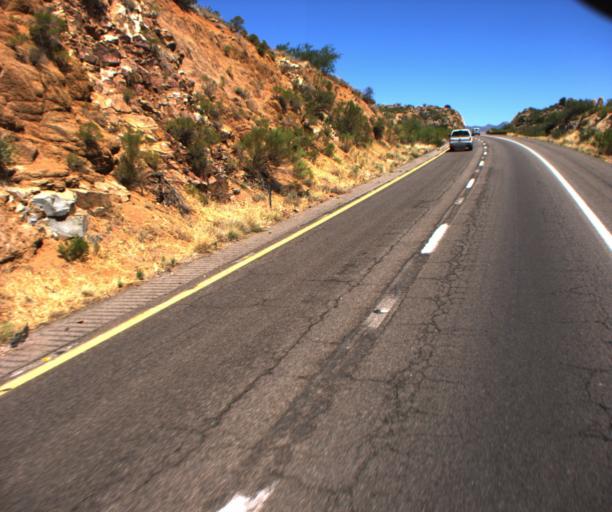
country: US
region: Arizona
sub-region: Gila County
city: Tonto Basin
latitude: 33.8433
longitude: -111.4679
